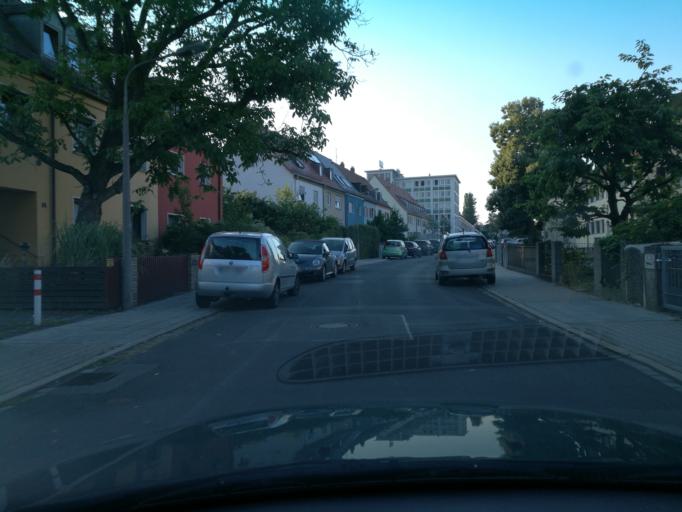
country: DE
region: Bavaria
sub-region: Regierungsbezirk Mittelfranken
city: Nuernberg
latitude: 49.4803
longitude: 11.1100
